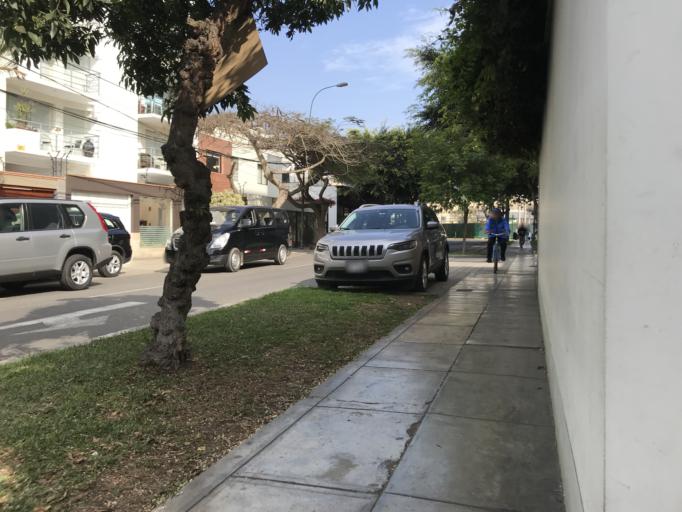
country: PE
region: Lima
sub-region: Lima
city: San Isidro
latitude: -12.1127
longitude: -77.0397
